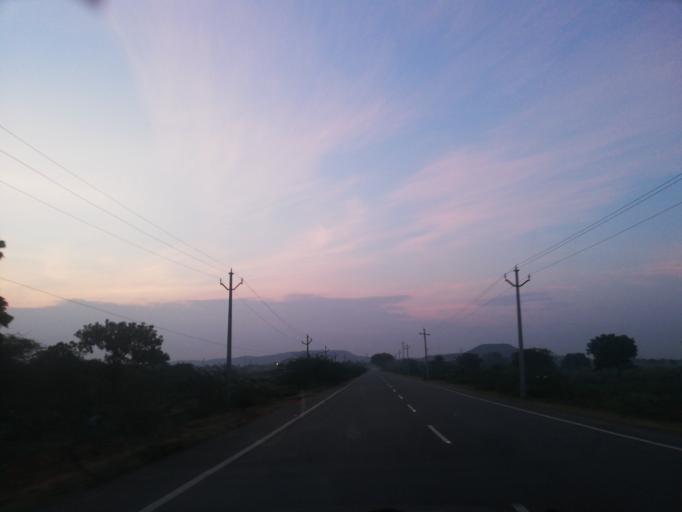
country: IN
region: Andhra Pradesh
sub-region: Guntur
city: Macherla
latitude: 16.6816
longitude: 79.2595
